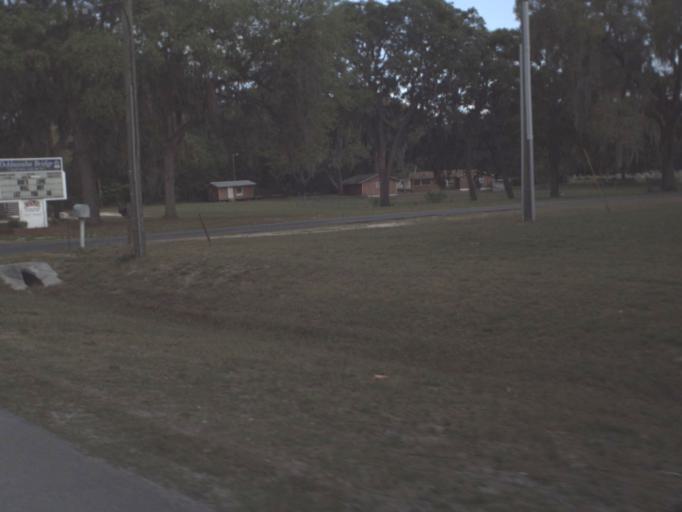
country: US
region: Florida
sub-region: Marion County
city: Silver Springs Shores
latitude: 29.1993
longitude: -81.9199
